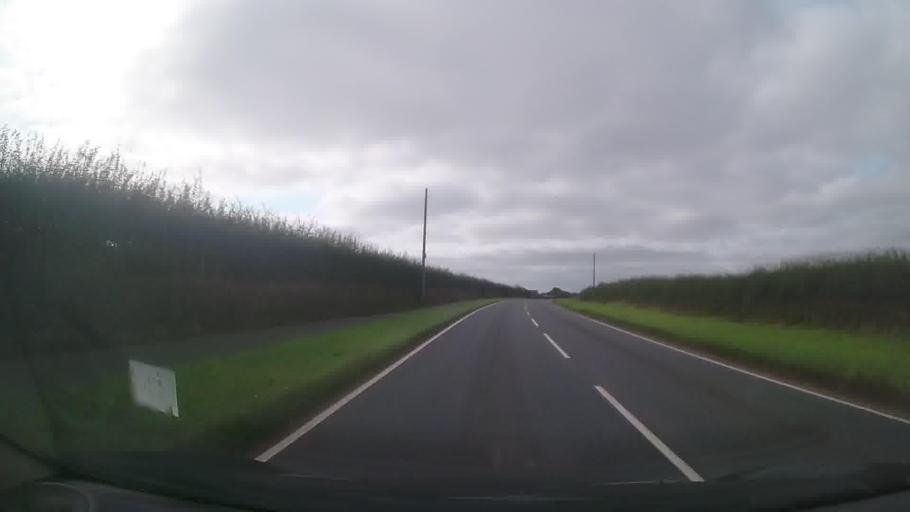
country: GB
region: Wales
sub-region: Pembrokeshire
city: Steynton
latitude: 51.7296
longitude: -5.0060
